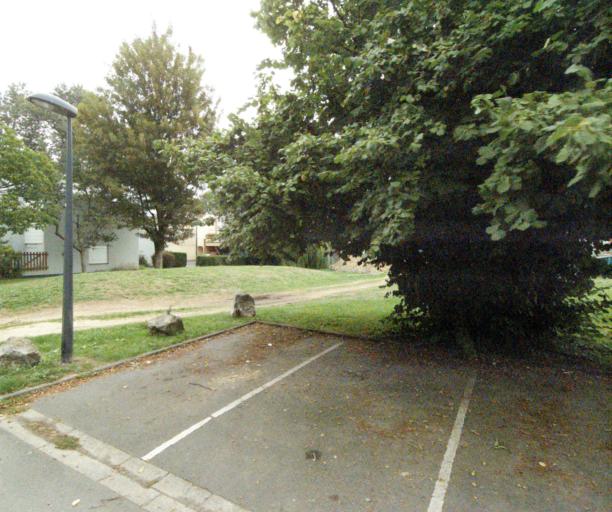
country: FR
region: Nord-Pas-de-Calais
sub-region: Departement du Nord
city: Mons-en-Baroeul
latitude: 50.6314
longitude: 3.1328
